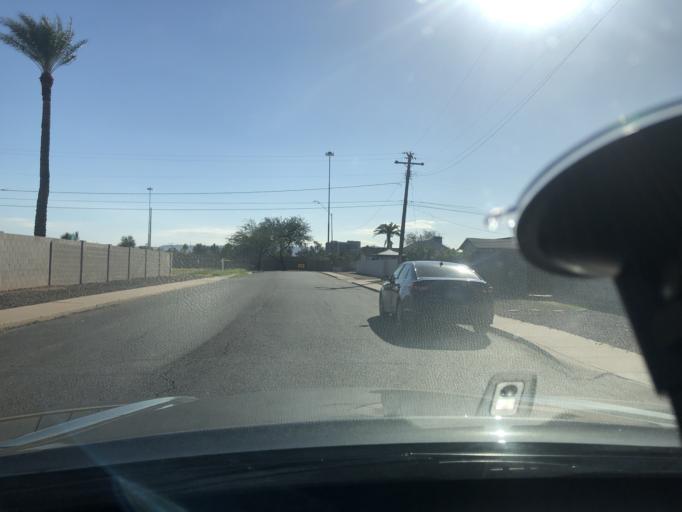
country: US
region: Arizona
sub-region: Maricopa County
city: Phoenix
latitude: 33.4638
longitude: -112.0412
